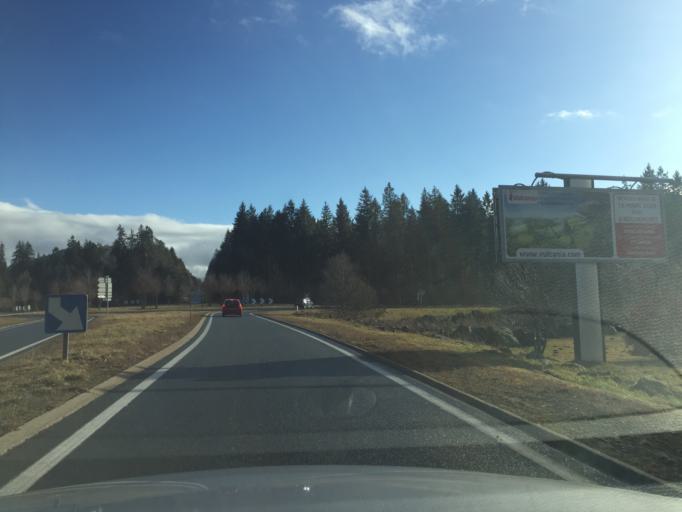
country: FR
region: Auvergne
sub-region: Departement du Puy-de-Dome
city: Orcines
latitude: 45.8141
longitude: 2.9514
